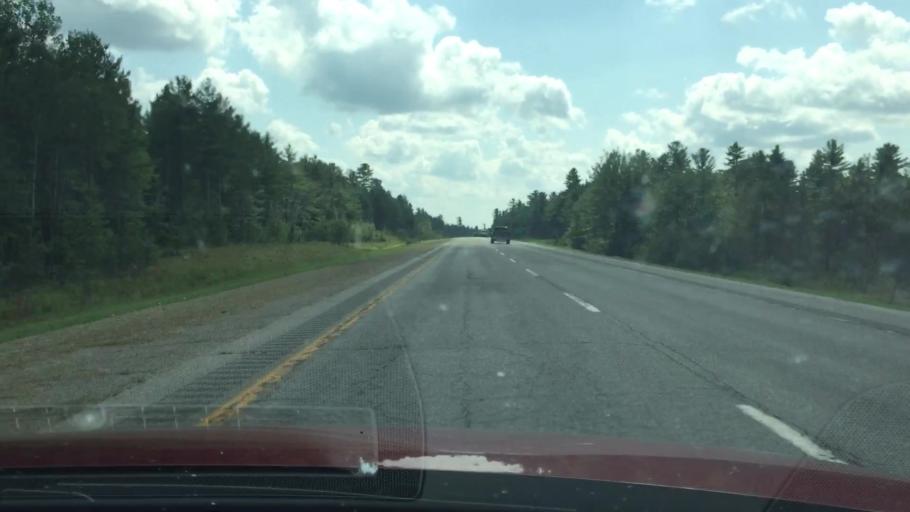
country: US
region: Maine
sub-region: Penobscot County
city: Medway
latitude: 45.5823
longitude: -68.5435
